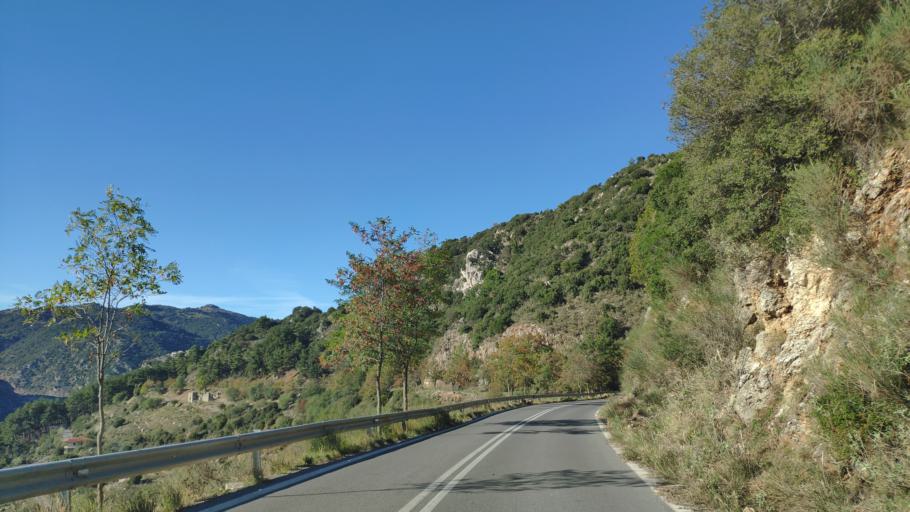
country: GR
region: Peloponnese
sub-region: Nomos Arkadias
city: Dimitsana
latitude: 37.5847
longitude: 22.0481
